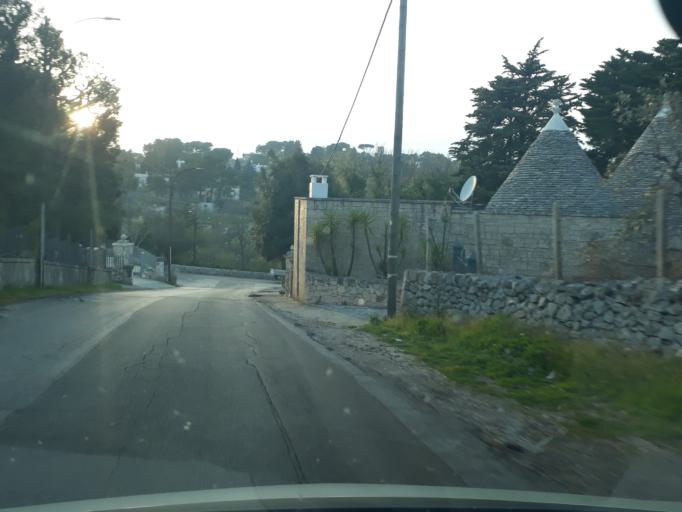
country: IT
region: Apulia
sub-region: Provincia di Brindisi
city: Lamie di Olimpie-Selva
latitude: 40.7991
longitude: 17.3533
